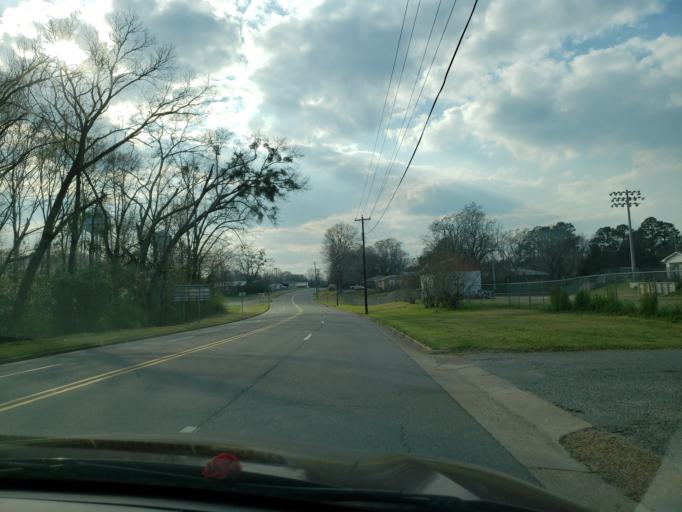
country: US
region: Alabama
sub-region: Hale County
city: Greensboro
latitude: 32.7007
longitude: -87.6014
